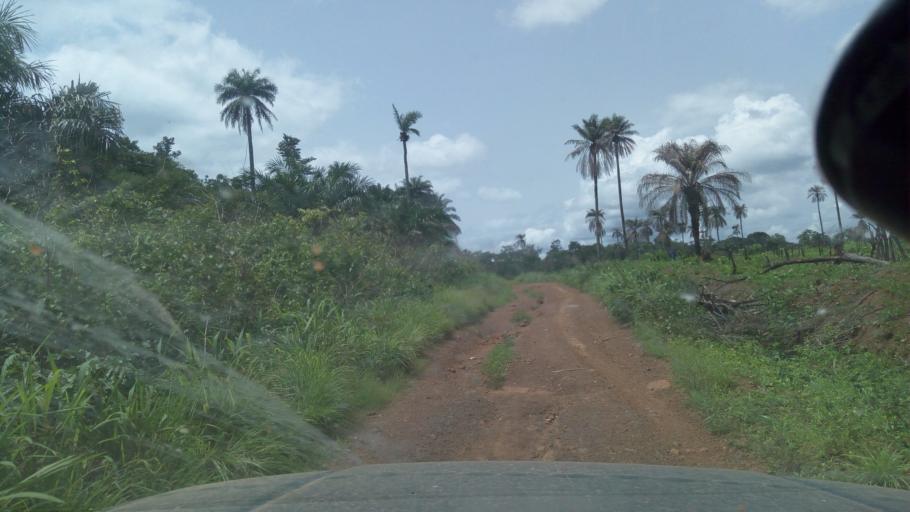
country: SL
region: Eastern Province
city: Segbwema
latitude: 7.9762
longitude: -11.0160
